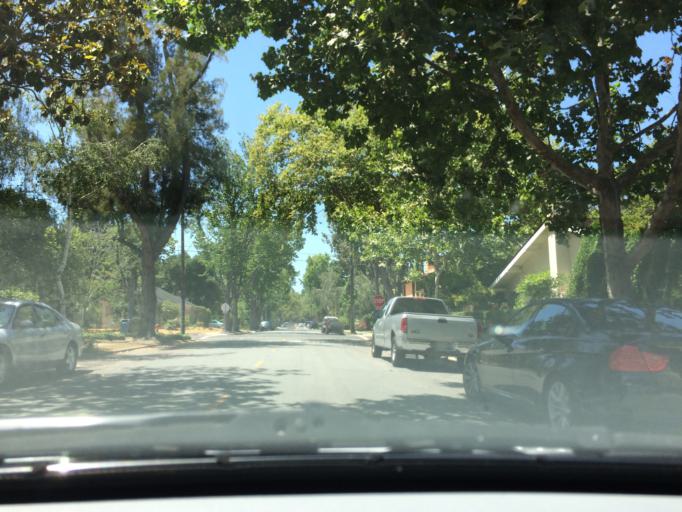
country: US
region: California
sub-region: Santa Clara County
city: Palo Alto
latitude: 37.4500
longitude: -122.1526
